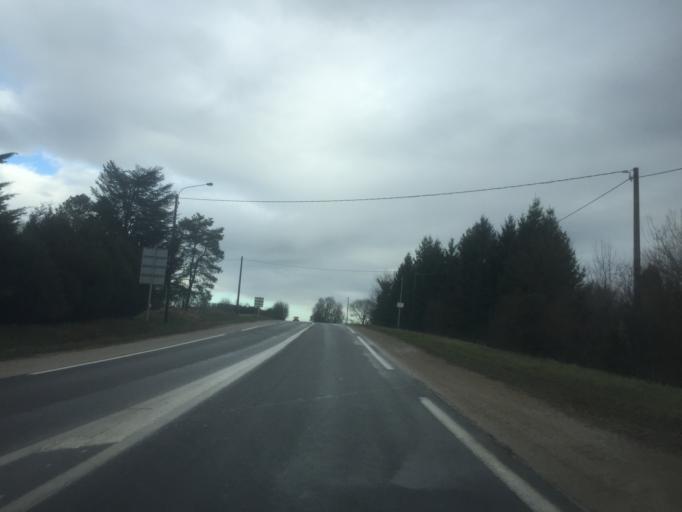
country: FR
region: Franche-Comte
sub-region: Departement du Jura
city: Fraisans
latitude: 47.1627
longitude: 5.7627
